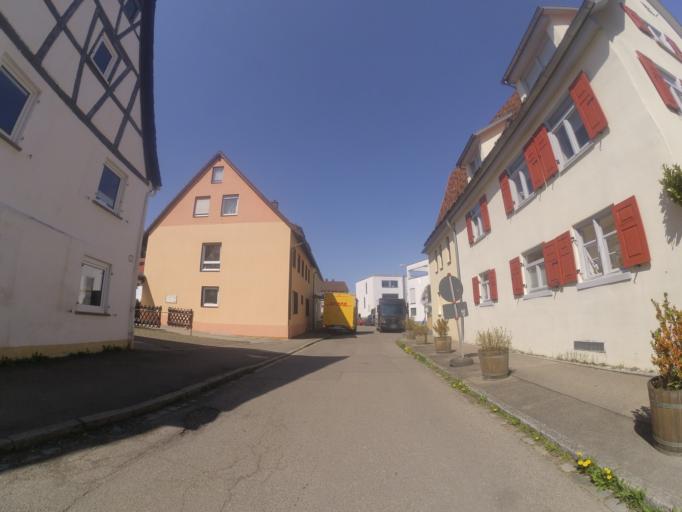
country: DE
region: Baden-Wuerttemberg
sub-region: Tuebingen Region
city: Ulm
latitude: 48.3962
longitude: 9.9575
